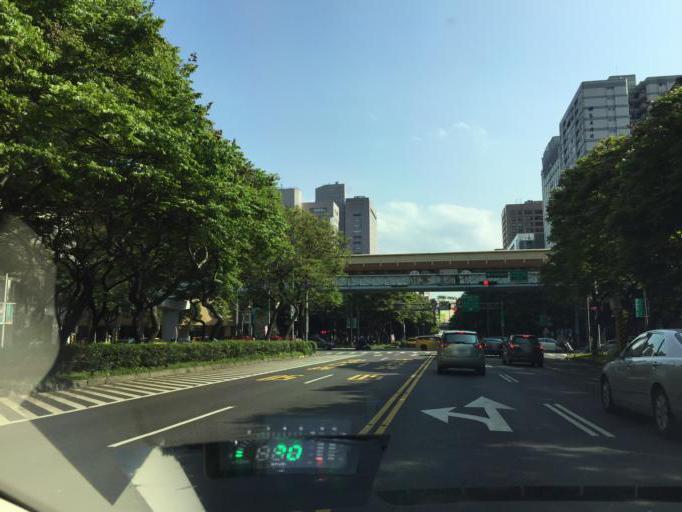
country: TW
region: Taipei
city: Taipei
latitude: 25.0254
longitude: 121.5487
